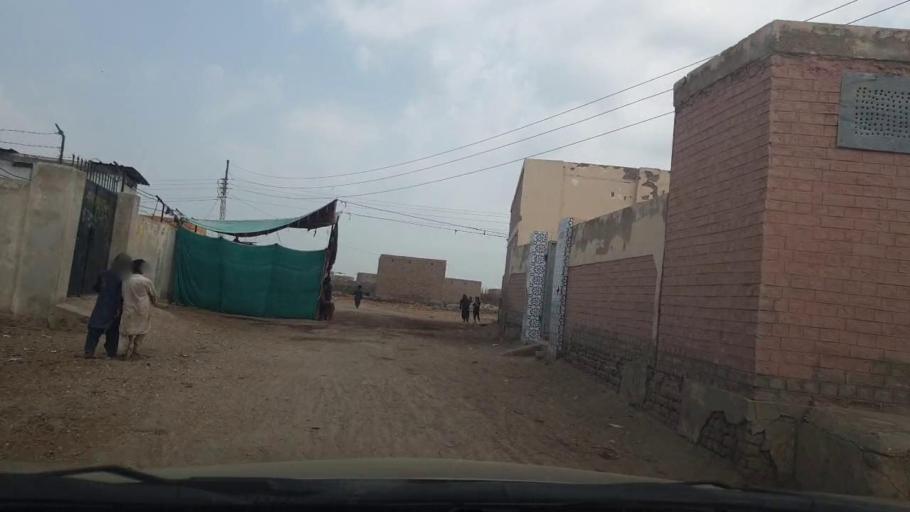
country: PK
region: Sindh
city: Ratodero
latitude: 27.7020
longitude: 68.2296
